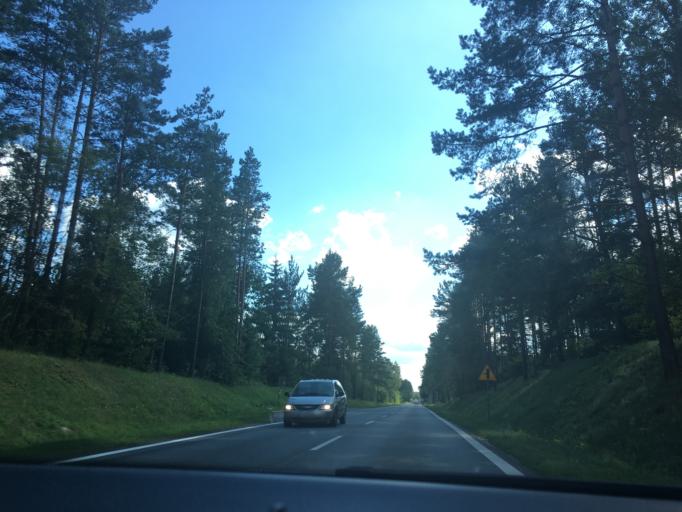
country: PL
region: Podlasie
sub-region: Powiat sokolski
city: Janow
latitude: 53.3617
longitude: 23.1047
